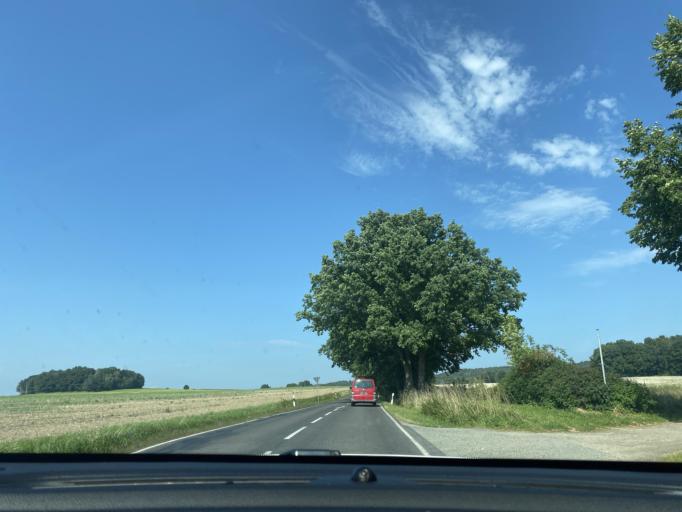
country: DE
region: Saxony
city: Reichenbach
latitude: 51.1512
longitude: 14.7964
